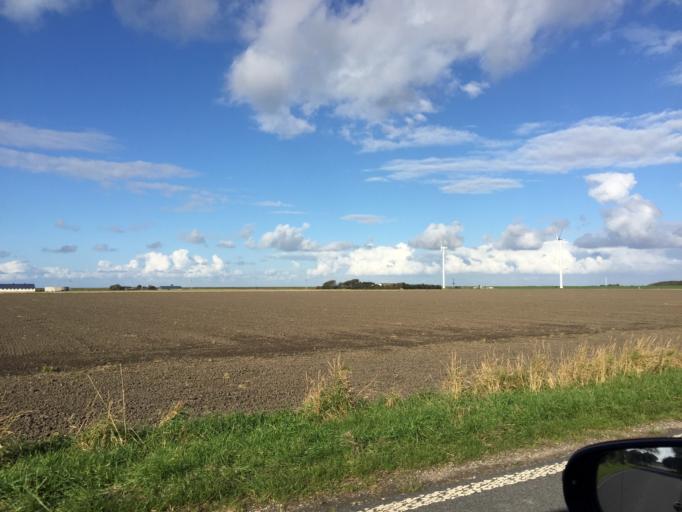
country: DE
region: Schleswig-Holstein
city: Friedrich-Wilhelm-Lubke-Koog
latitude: 54.8693
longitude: 8.6283
